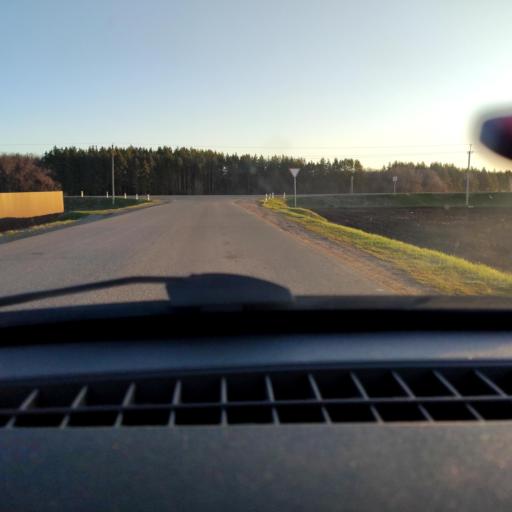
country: RU
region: Bashkortostan
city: Avdon
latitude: 54.5595
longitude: 55.6688
